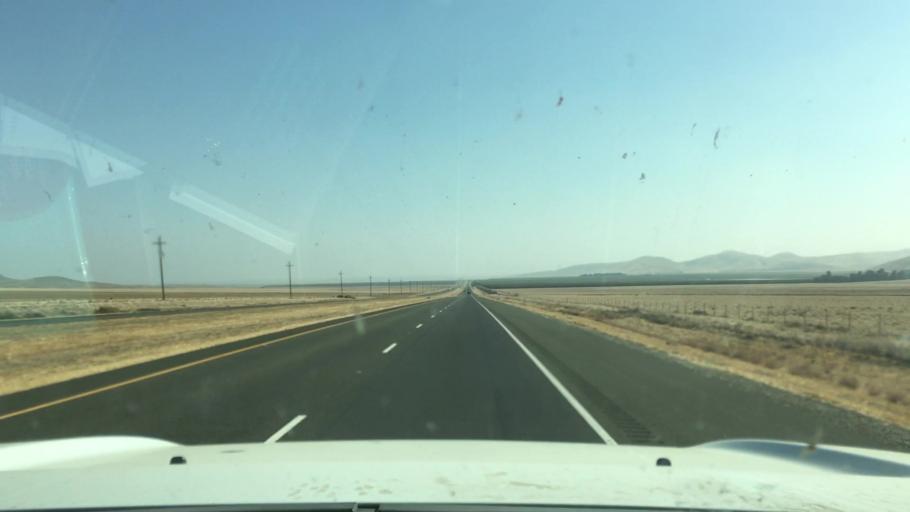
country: US
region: California
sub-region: San Luis Obispo County
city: Shandon
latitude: 35.6940
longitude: -120.1303
